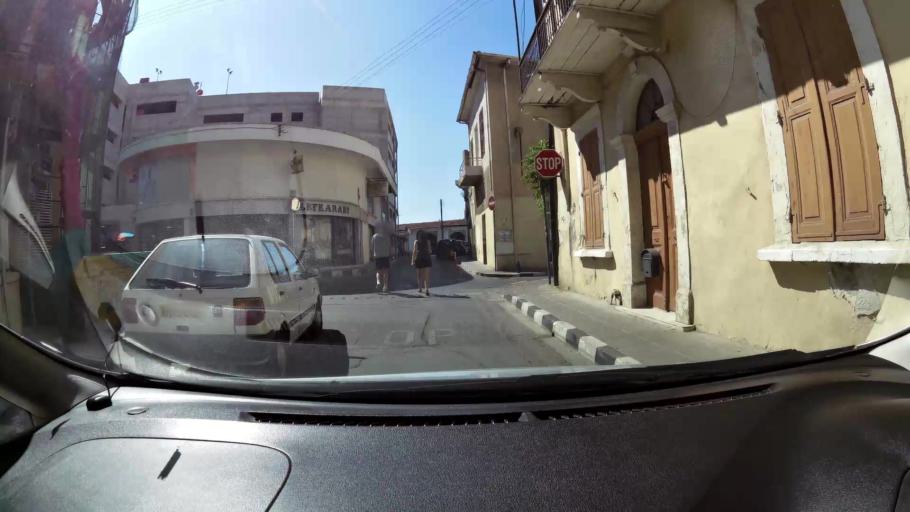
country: CY
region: Larnaka
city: Larnaca
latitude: 34.9128
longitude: 33.6366
